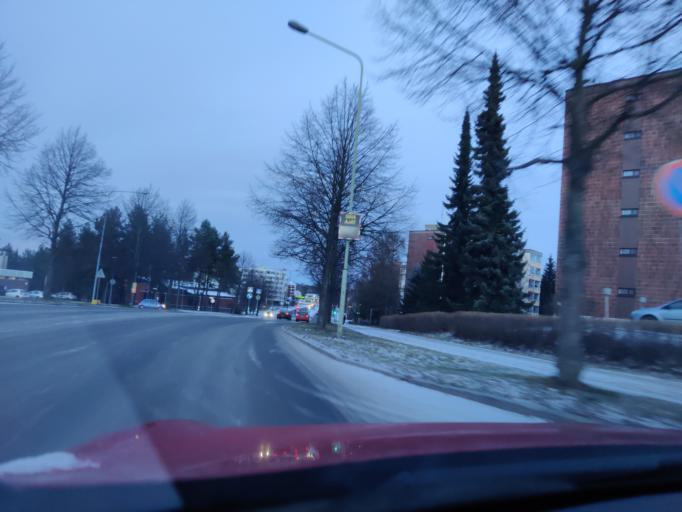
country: FI
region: Pirkanmaa
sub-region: Tampere
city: Nokia
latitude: 61.4779
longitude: 23.5143
